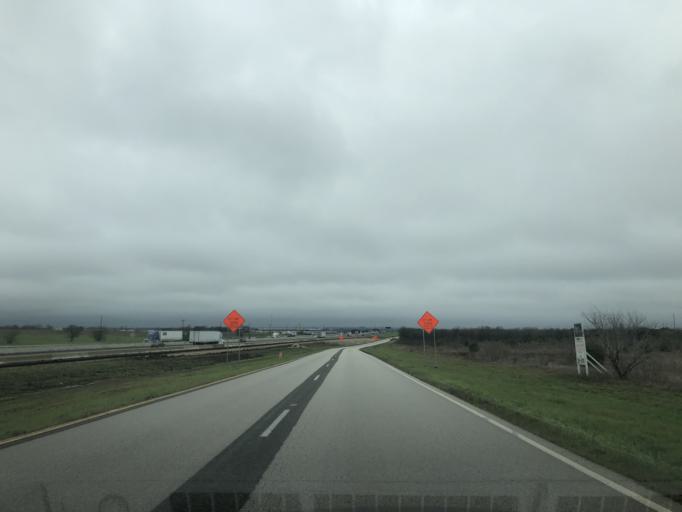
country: US
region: Texas
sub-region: Williamson County
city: Serenada
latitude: 30.7348
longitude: -97.6409
